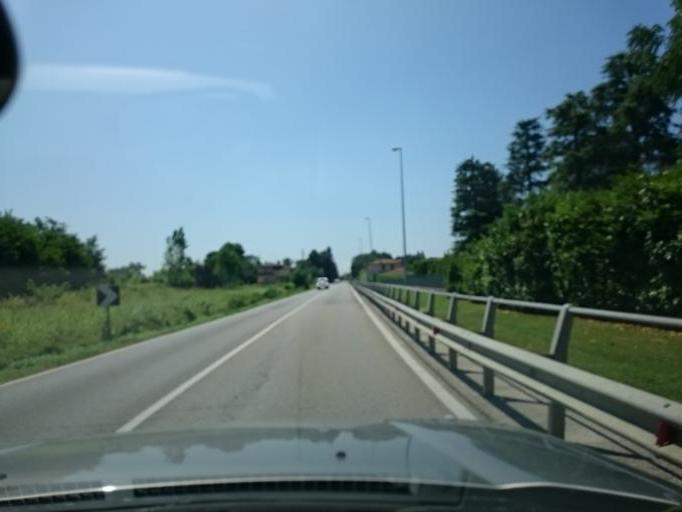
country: IT
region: Veneto
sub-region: Provincia di Padova
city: Villaguattera
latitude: 45.4348
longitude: 11.8274
